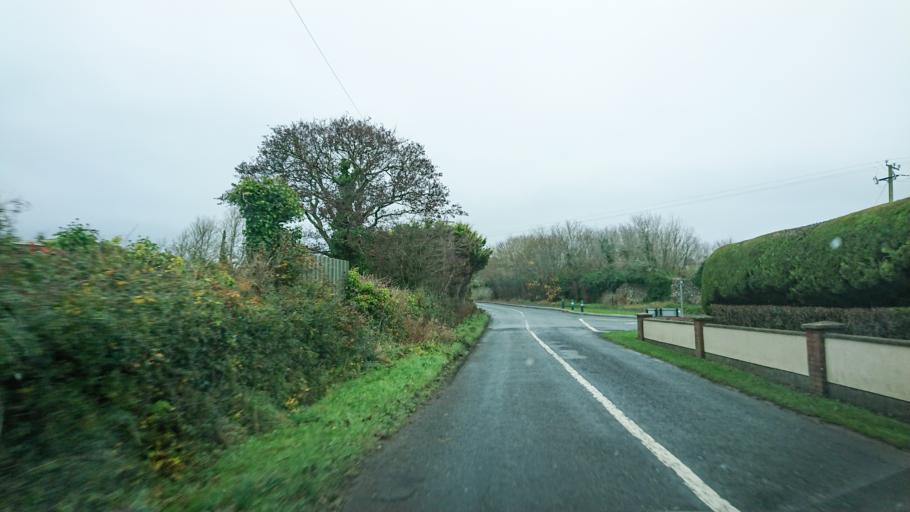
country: IE
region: Munster
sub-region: Waterford
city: Tra Mhor
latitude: 52.1479
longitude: -7.1726
